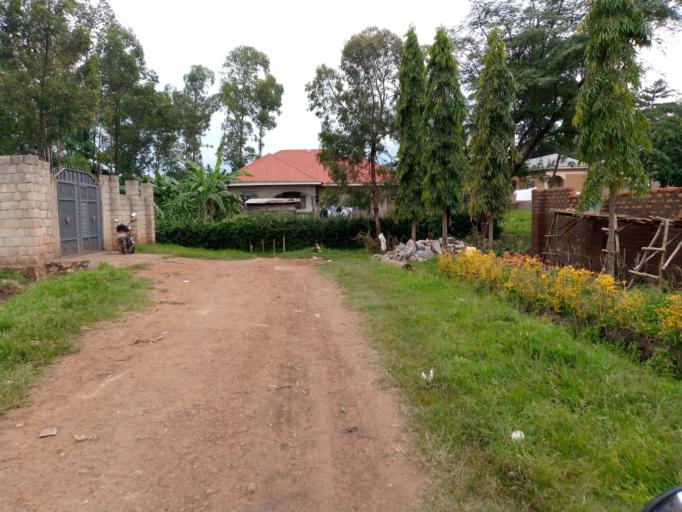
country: UG
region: Eastern Region
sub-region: Mbale District
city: Mbale
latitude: 1.0847
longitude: 34.1754
